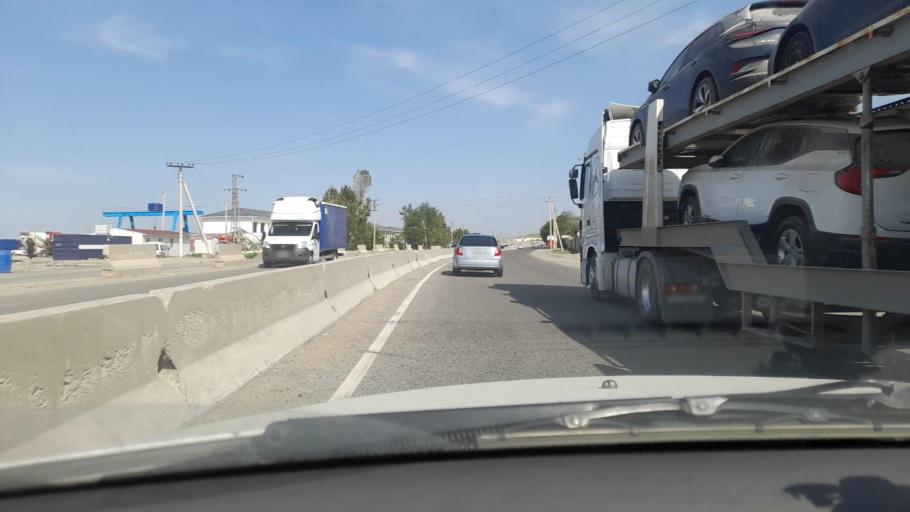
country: UZ
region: Samarqand
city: Samarqand
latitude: 39.7017
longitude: 67.0108
